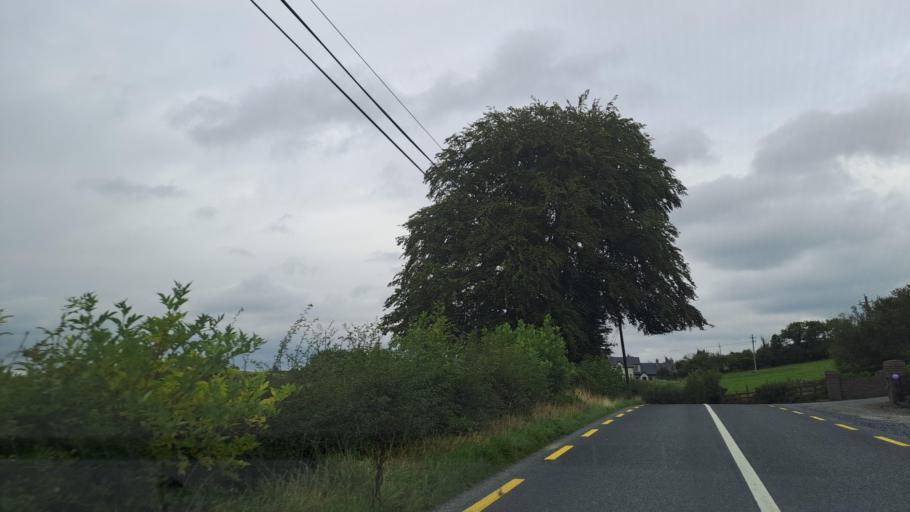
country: IE
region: Ulster
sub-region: An Cabhan
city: Bailieborough
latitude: 53.9489
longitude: -6.9524
